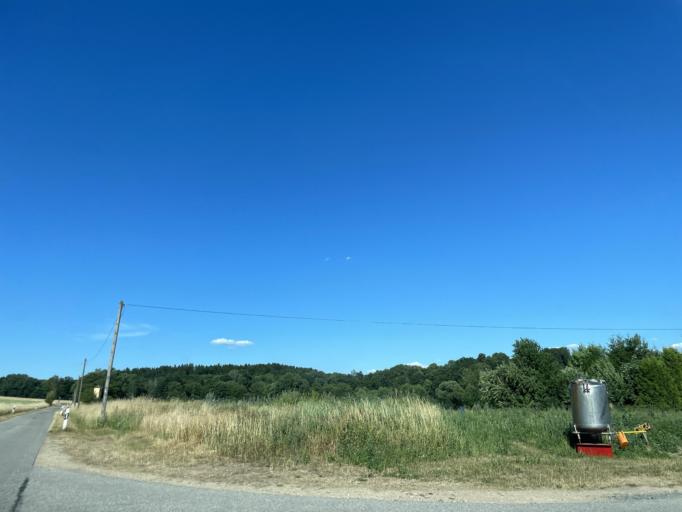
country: DE
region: Bavaria
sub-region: Upper Palatinate
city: Trabitz
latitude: 49.7864
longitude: 11.9197
